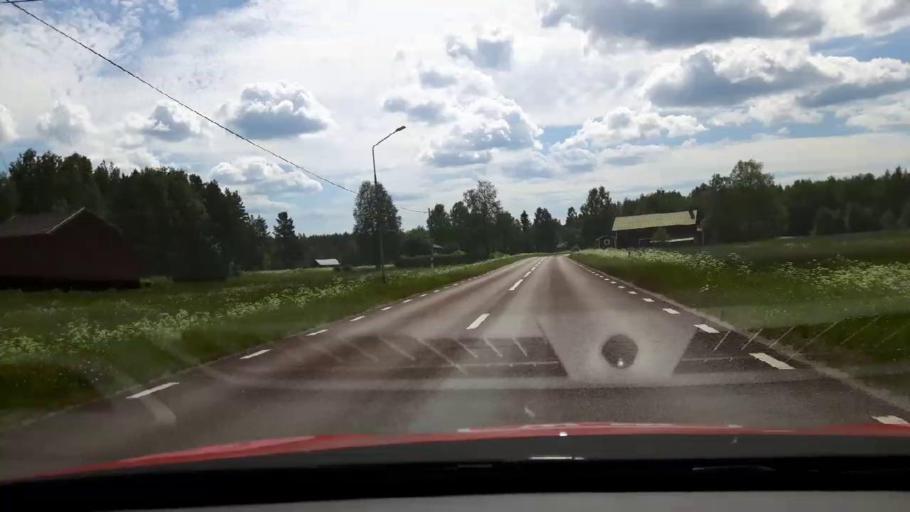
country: SE
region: Jaemtland
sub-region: Harjedalens Kommun
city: Sveg
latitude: 62.1580
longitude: 14.9526
